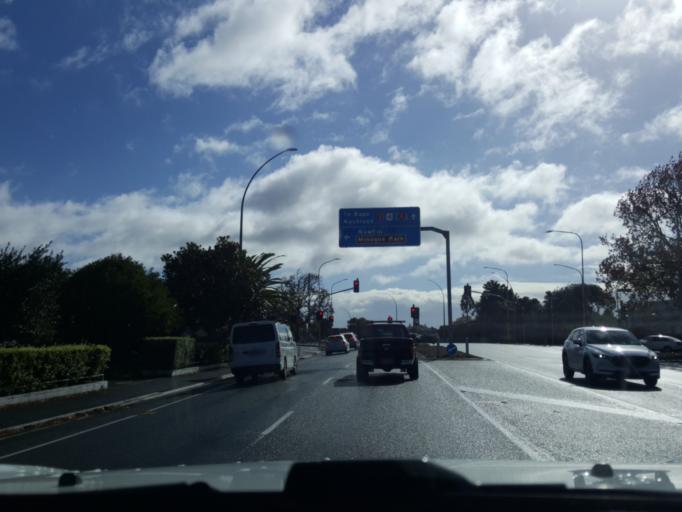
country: NZ
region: Waikato
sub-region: Hamilton City
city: Hamilton
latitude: -37.7703
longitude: 175.2629
